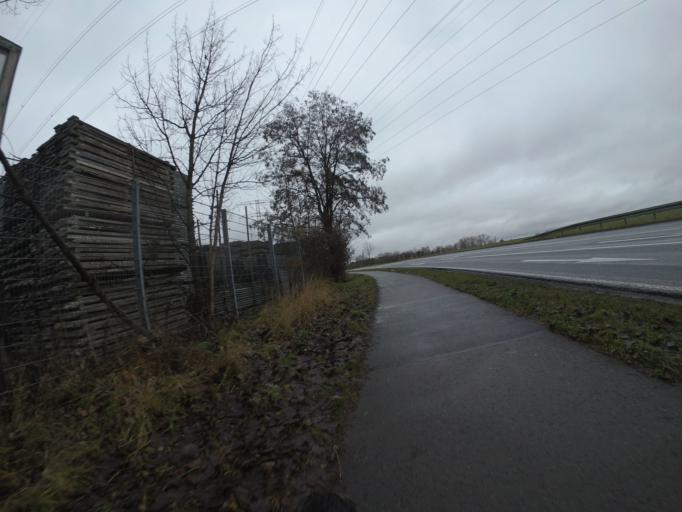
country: DE
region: Berlin
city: Marzahn
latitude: 52.5544
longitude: 13.5910
